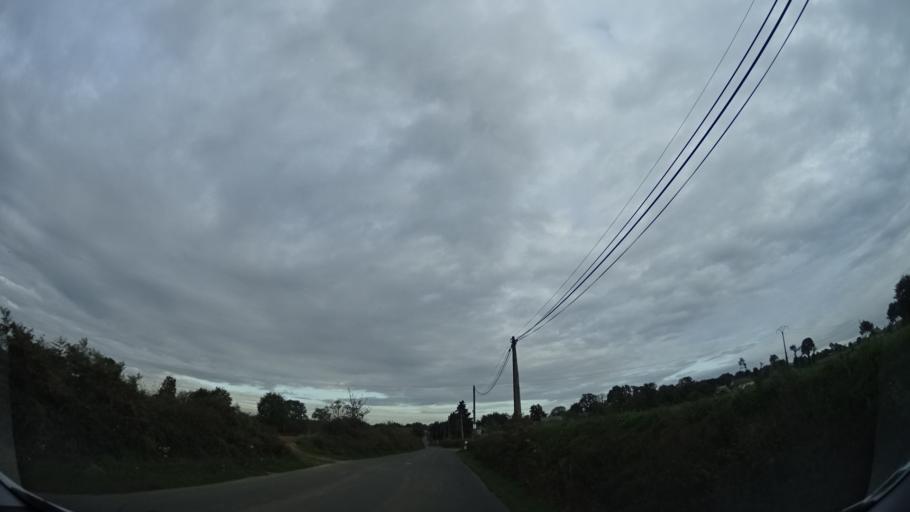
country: FR
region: Brittany
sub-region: Departement d'Ille-et-Vilaine
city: Geveze
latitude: 48.2259
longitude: -1.7860
